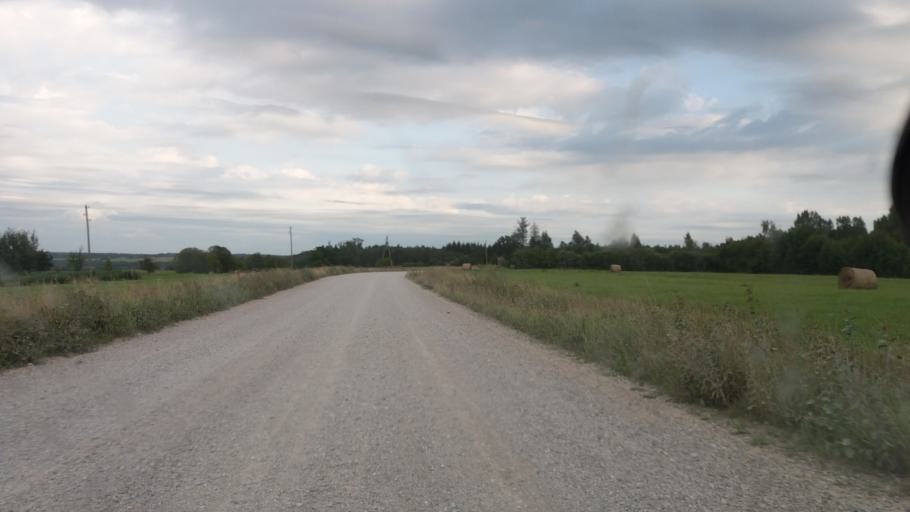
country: LV
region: Talsu Rajons
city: Sabile
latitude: 57.0256
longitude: 22.5842
